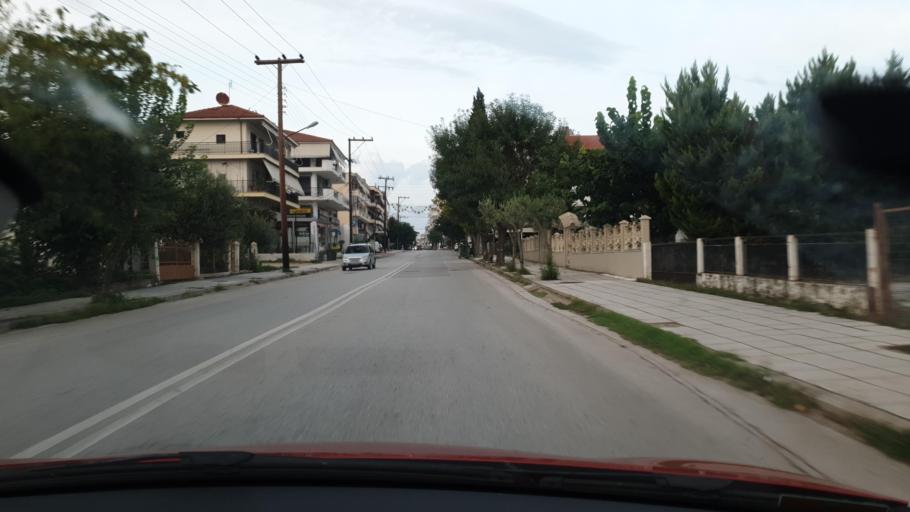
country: GR
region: Central Macedonia
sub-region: Nomos Kilkis
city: Kilkis
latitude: 40.9870
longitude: 22.8667
